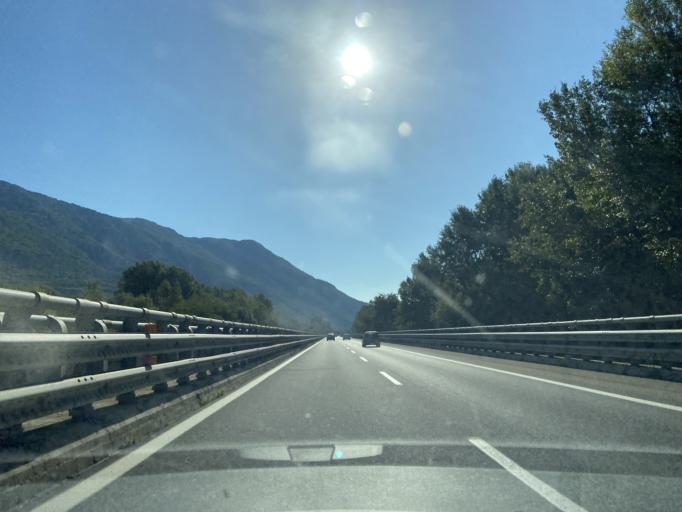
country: IT
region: Piedmont
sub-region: Provincia di Torino
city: San Didero
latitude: 45.1245
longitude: 7.2100
